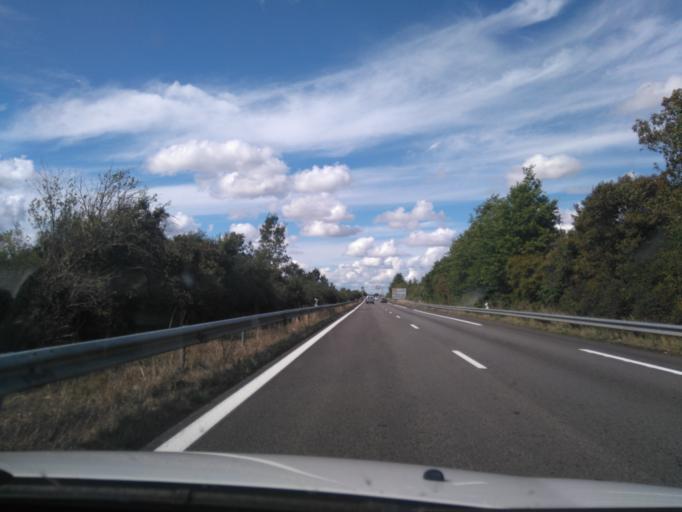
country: FR
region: Pays de la Loire
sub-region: Departement de la Loire-Atlantique
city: Heric
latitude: 47.4322
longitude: -1.6381
